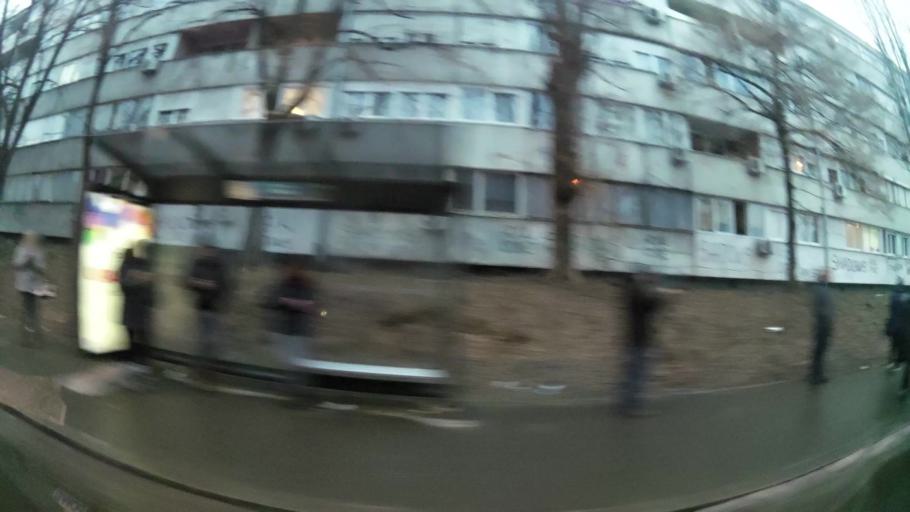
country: RS
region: Central Serbia
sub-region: Belgrade
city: Vozdovac
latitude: 44.7713
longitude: 20.4880
